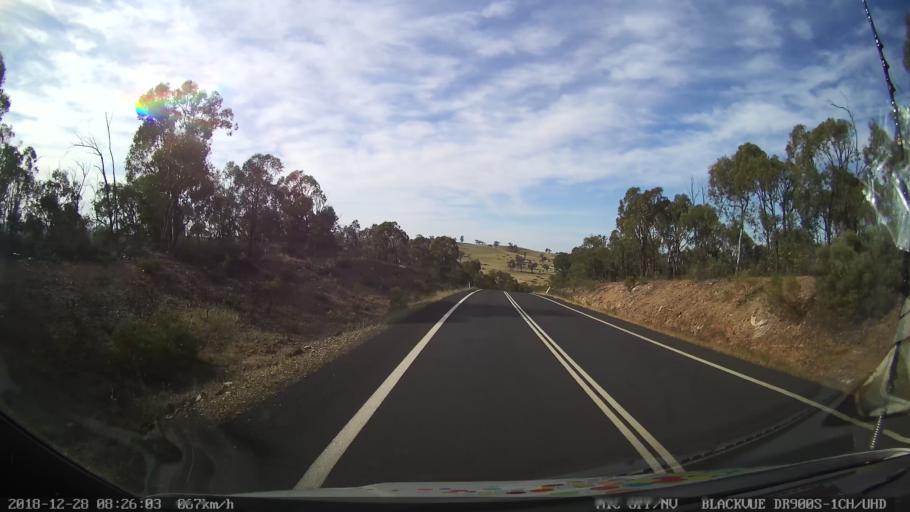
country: AU
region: New South Wales
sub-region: Blayney
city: Blayney
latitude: -33.9320
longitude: 149.3498
